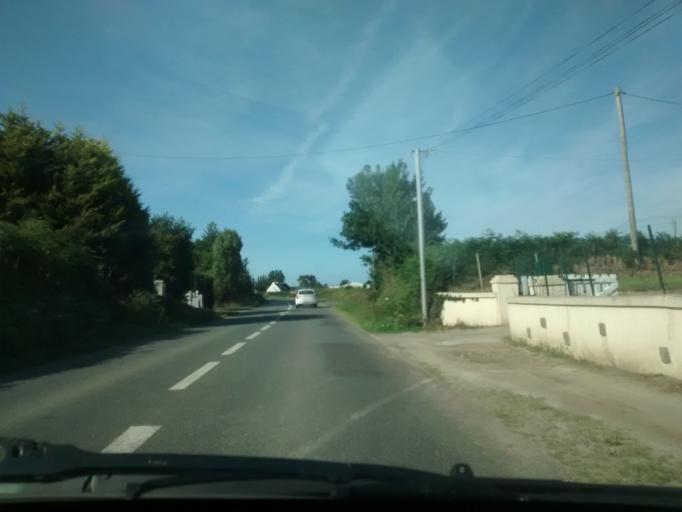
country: FR
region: Brittany
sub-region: Departement des Cotes-d'Armor
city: Penvenan
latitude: 48.8026
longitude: -3.3091
